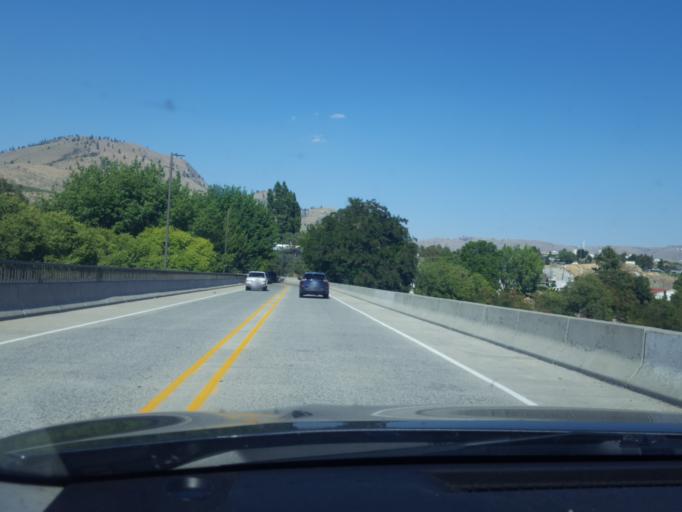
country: US
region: Washington
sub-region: Chelan County
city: Chelan
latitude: 47.8360
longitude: -120.0167
